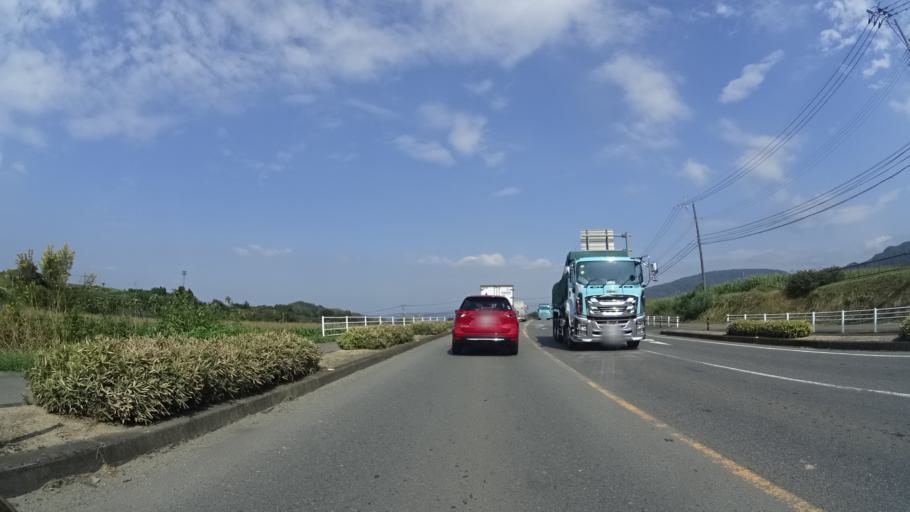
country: JP
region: Kumamoto
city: Kumamoto
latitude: 32.7491
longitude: 130.7999
